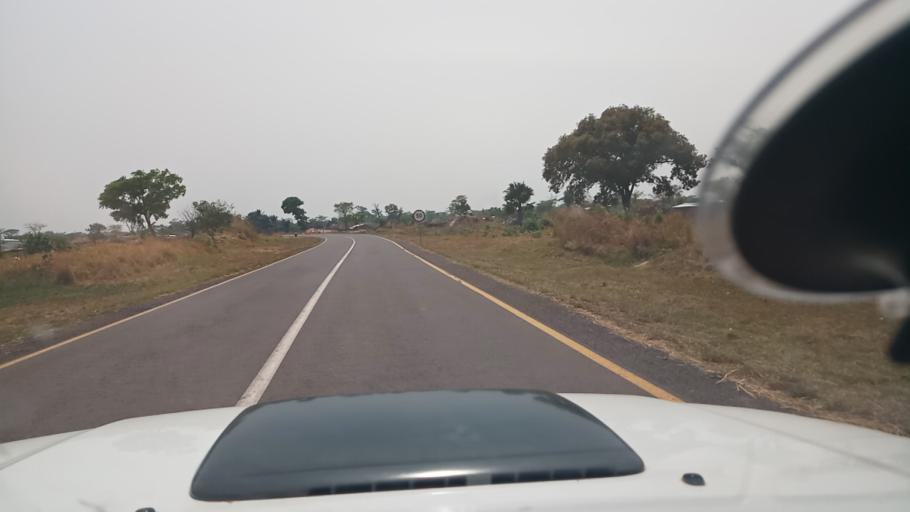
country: ZM
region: Luapula
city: Mwense
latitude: -10.7923
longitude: 28.2328
